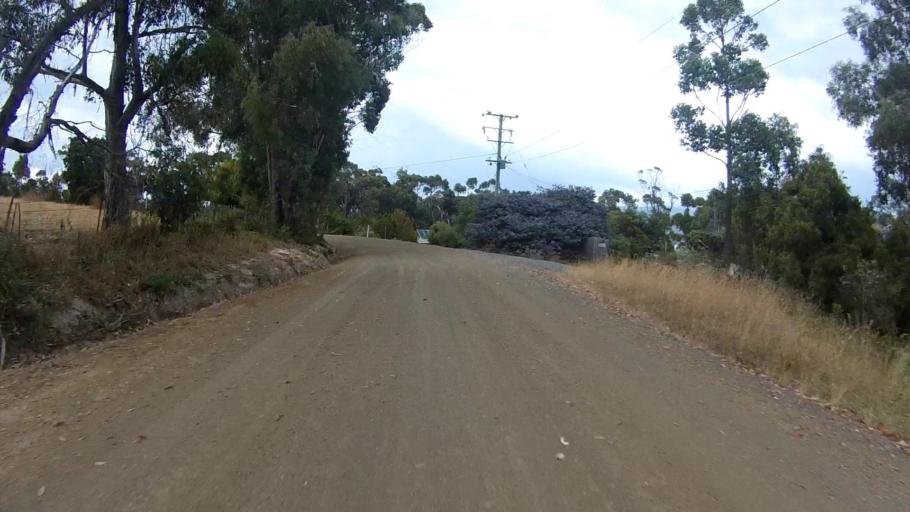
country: AU
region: Tasmania
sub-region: Huon Valley
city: Cygnet
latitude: -43.2328
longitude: 147.0983
